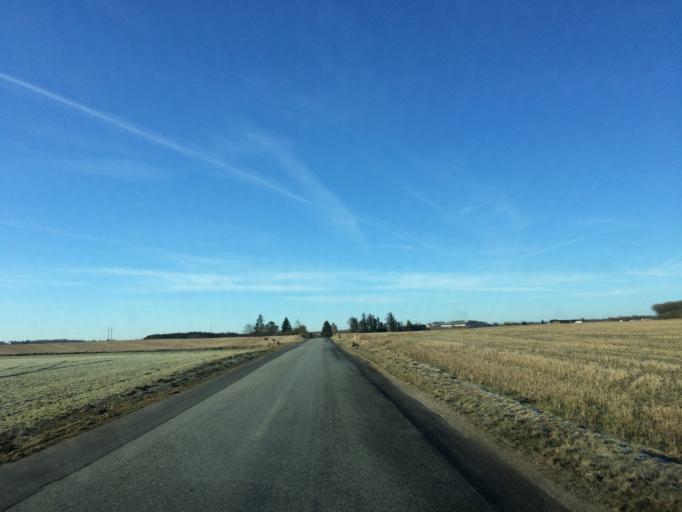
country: DK
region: North Denmark
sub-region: Mariagerfjord Kommune
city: Hobro
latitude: 56.6074
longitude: 9.6342
